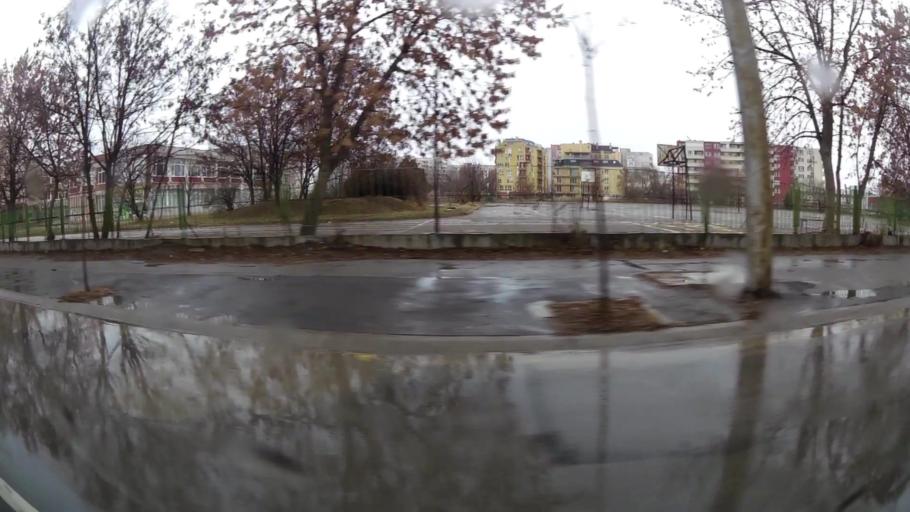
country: BG
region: Sofia-Capital
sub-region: Stolichna Obshtina
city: Sofia
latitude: 42.6440
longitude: 23.4049
